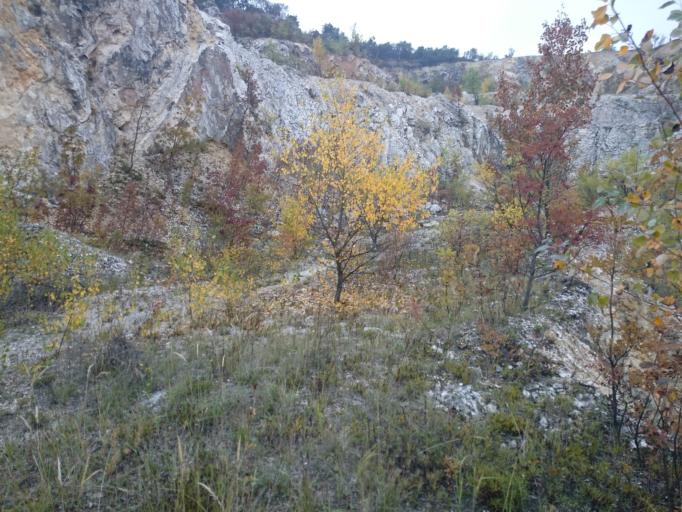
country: HU
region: Komarom-Esztergom
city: Piliscsev
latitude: 47.6608
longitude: 18.8057
